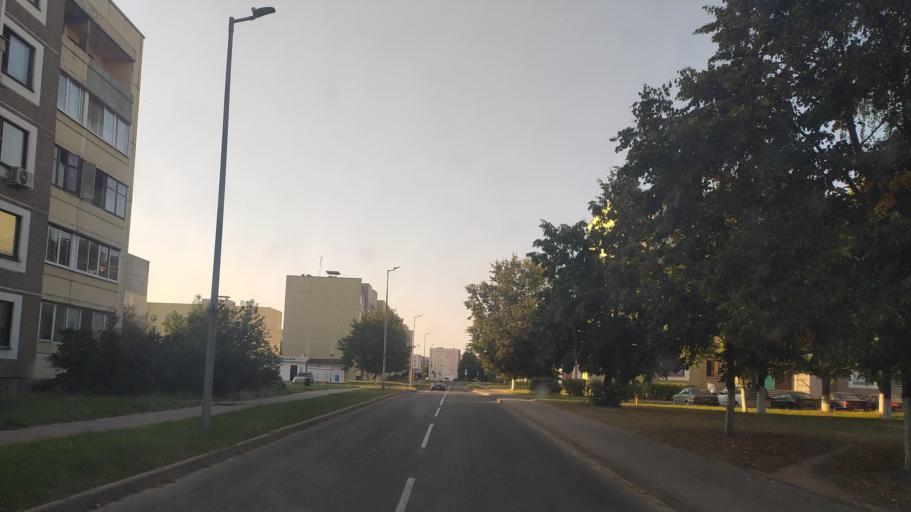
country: BY
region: Brest
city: Byaroza
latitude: 52.5467
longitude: 24.9842
